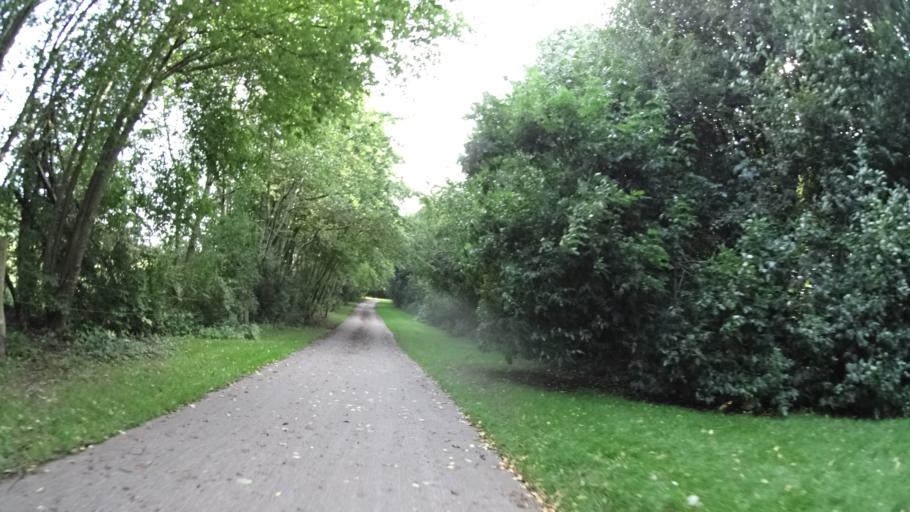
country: DK
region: Central Jutland
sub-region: Arhus Kommune
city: Stavtrup
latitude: 56.1339
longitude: 10.1314
